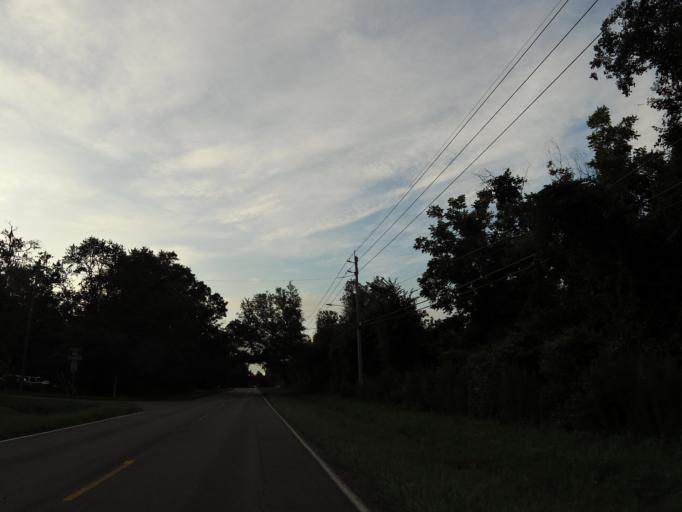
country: US
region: Florida
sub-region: Nassau County
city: Nassau Village-Ratliff
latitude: 30.3692
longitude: -81.8069
